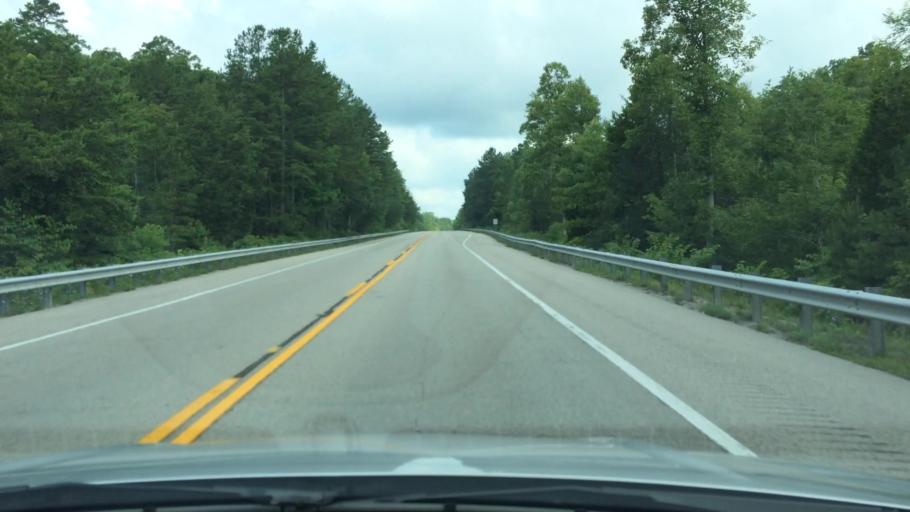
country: US
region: Kentucky
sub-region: McCreary County
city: Whitley City
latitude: 36.9064
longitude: -84.5058
